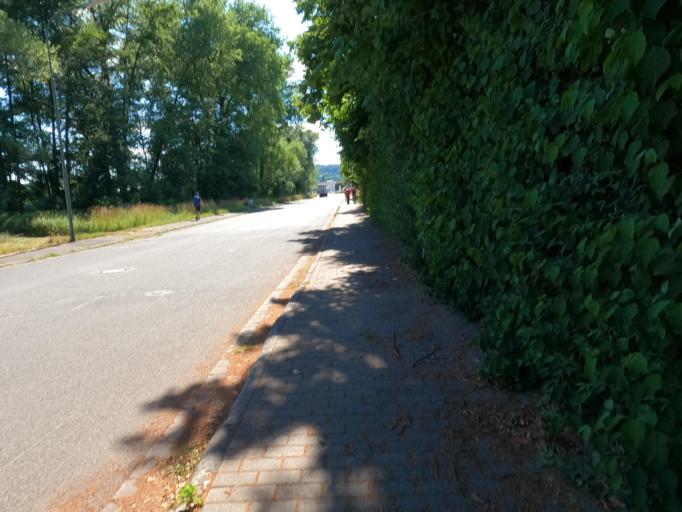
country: DE
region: Hesse
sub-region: Regierungsbezirk Darmstadt
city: Schluchtern
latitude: 50.3559
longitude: 9.5414
